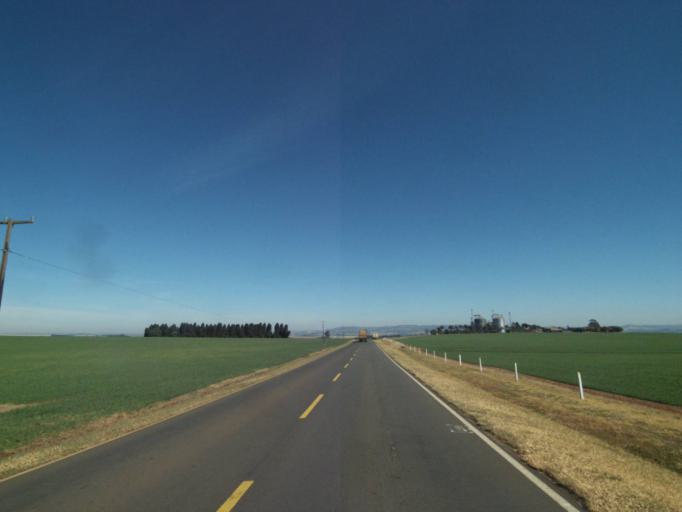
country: BR
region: Parana
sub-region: Tibagi
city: Tibagi
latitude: -24.5209
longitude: -50.3521
